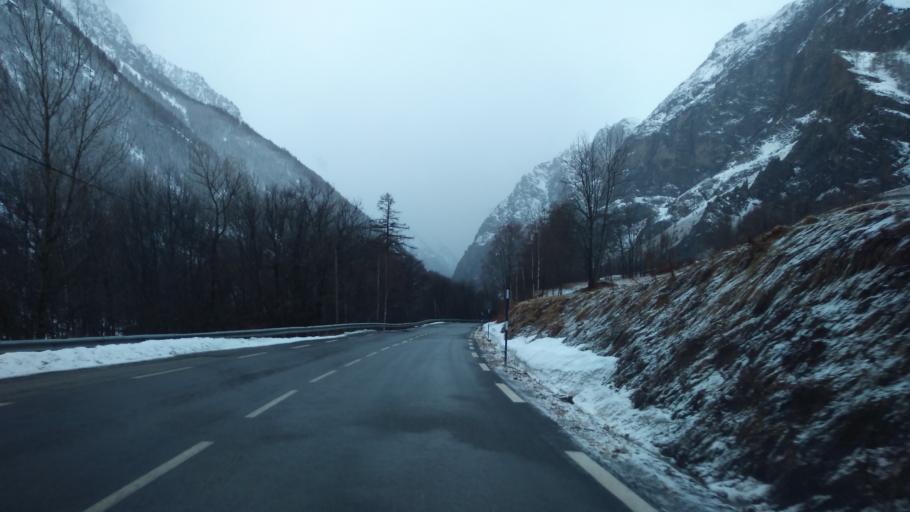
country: FR
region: Rhone-Alpes
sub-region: Departement de l'Isere
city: Mont-de-Lans
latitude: 45.0435
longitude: 6.2928
